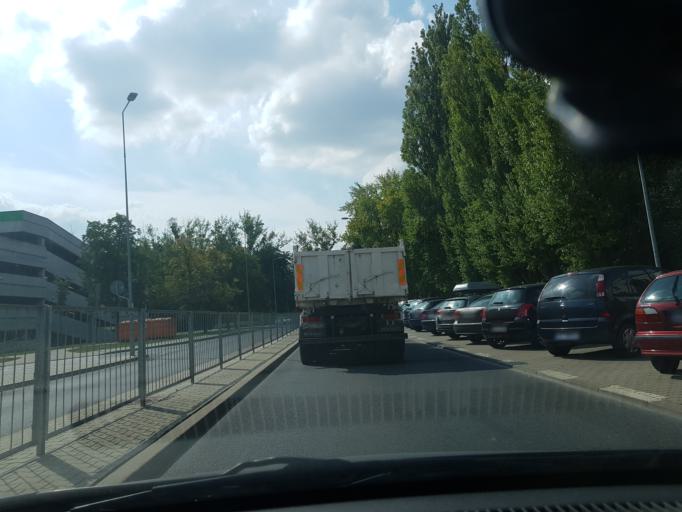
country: PL
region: Masovian Voivodeship
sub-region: Warszawa
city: Bielany
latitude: 52.2914
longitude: 20.9271
